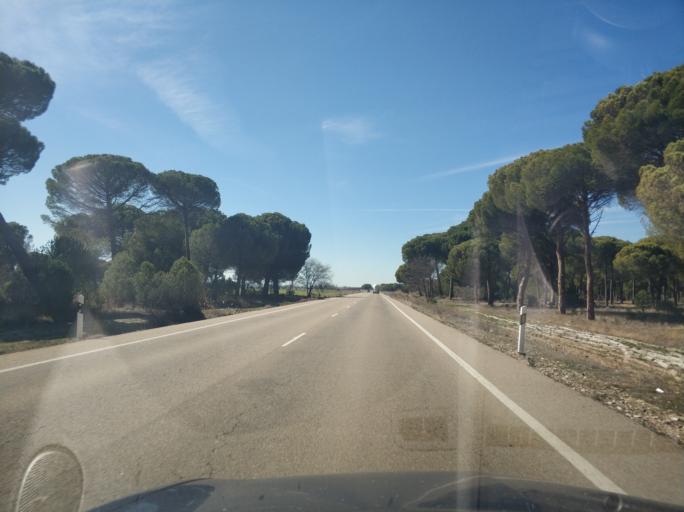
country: ES
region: Castille and Leon
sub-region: Provincia de Valladolid
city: Tudela de Duero
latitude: 41.5612
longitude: -4.6170
